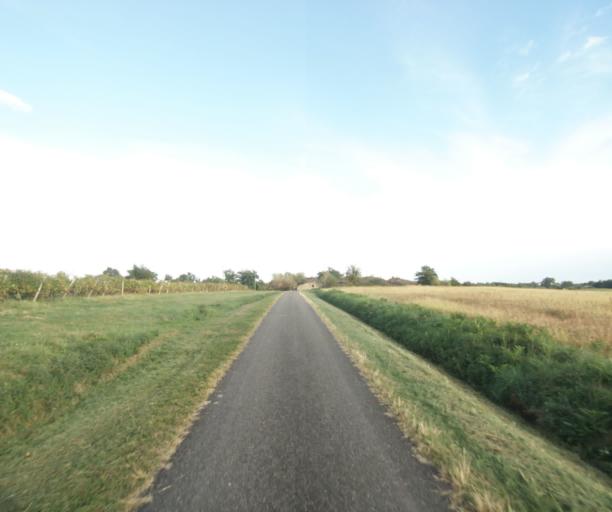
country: FR
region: Midi-Pyrenees
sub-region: Departement du Gers
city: Le Houga
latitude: 43.8496
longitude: -0.1279
